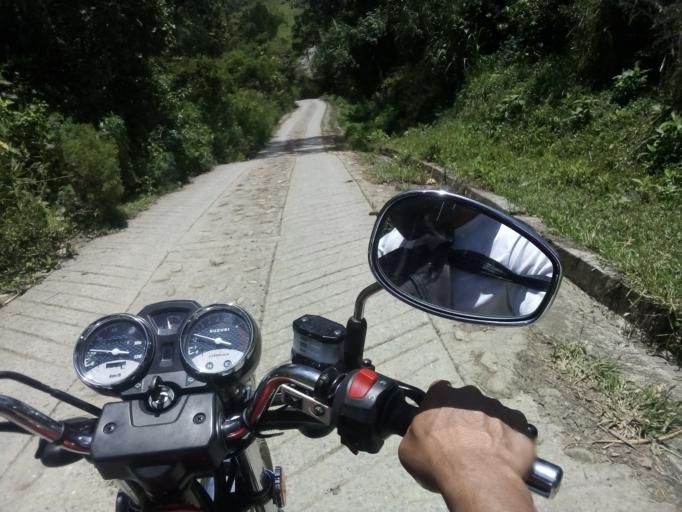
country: CO
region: Santander
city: Guepsa
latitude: 6.0129
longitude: -73.5538
